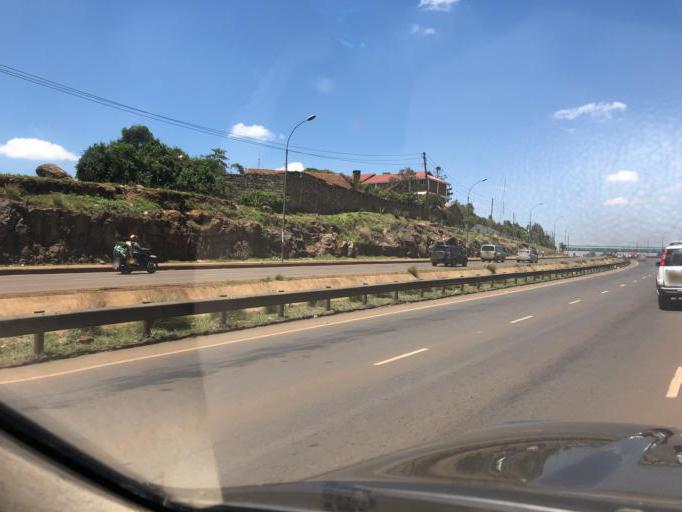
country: KE
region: Kiambu
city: Kiambu
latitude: -1.2143
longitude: 36.8979
